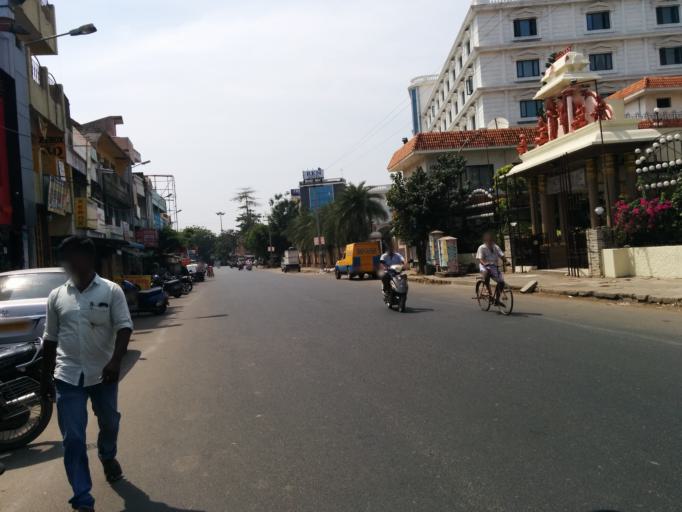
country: IN
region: Pondicherry
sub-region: Puducherry
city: Puducherry
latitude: 11.9419
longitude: 79.8295
